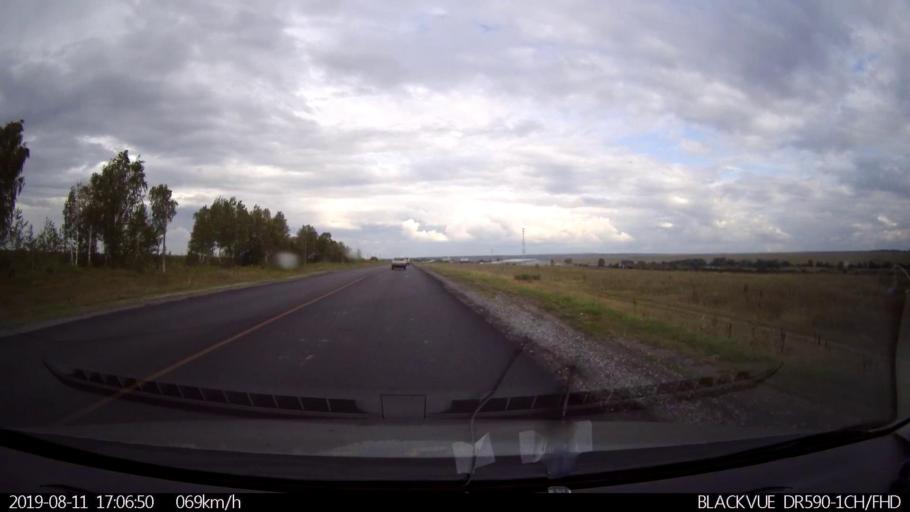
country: RU
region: Ulyanovsk
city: Mayna
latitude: 54.2939
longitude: 47.8130
